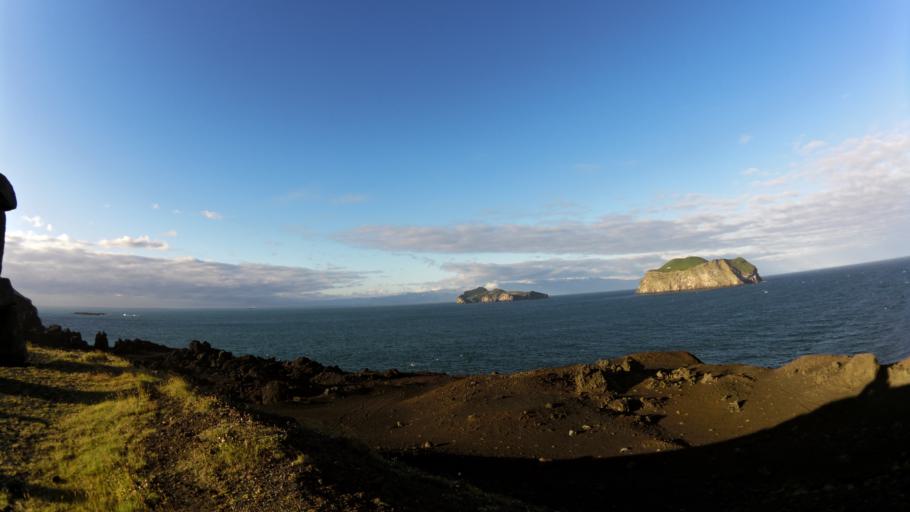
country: IS
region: South
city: Vestmannaeyjar
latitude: 63.4426
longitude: -20.2369
